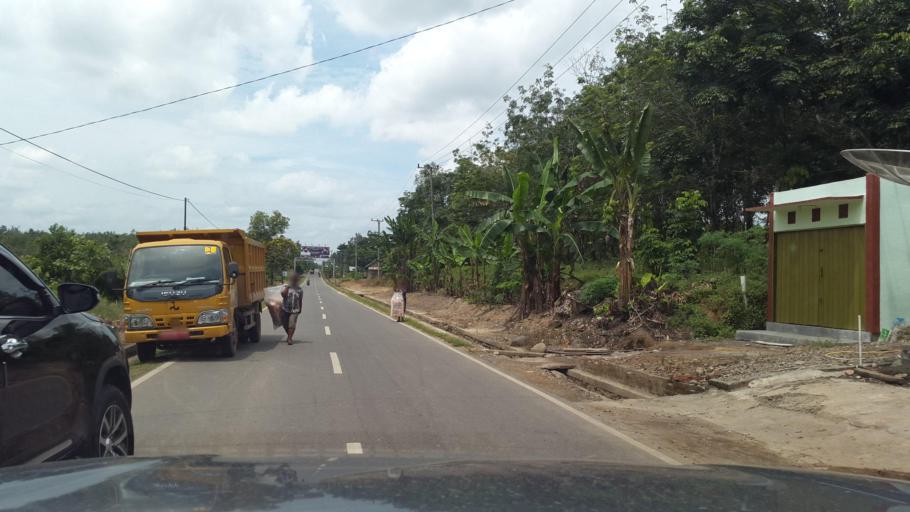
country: ID
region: South Sumatra
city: Gunungmegang Dalam
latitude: -3.3135
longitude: 103.8871
